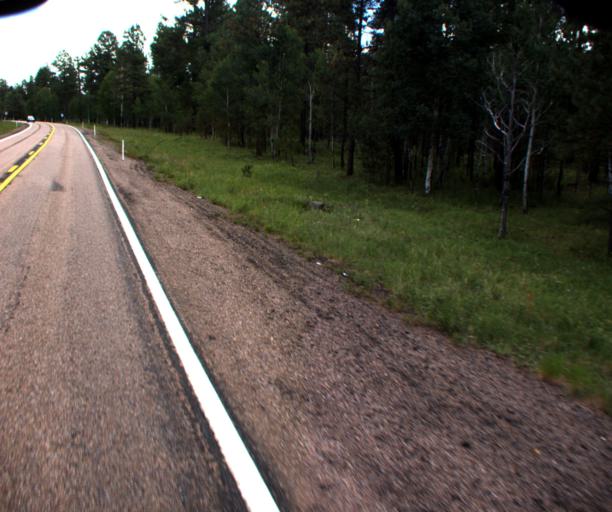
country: US
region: Arizona
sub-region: Navajo County
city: Pinetop-Lakeside
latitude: 34.0446
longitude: -109.7095
